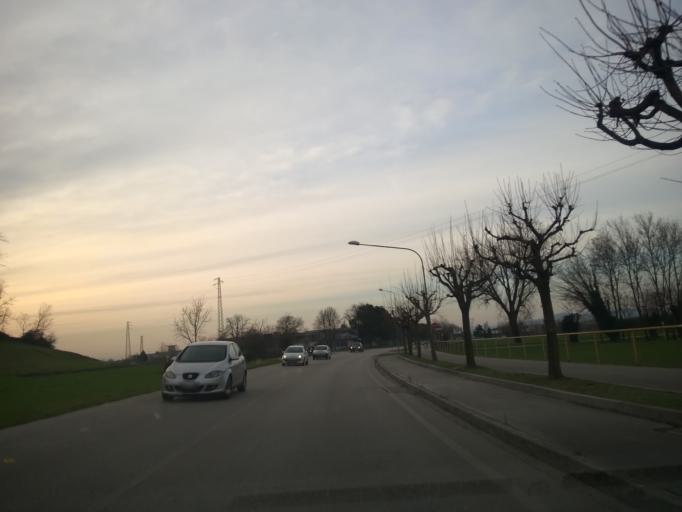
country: IT
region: Veneto
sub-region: Provincia di Vicenza
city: Carre
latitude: 45.7382
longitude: 11.4642
